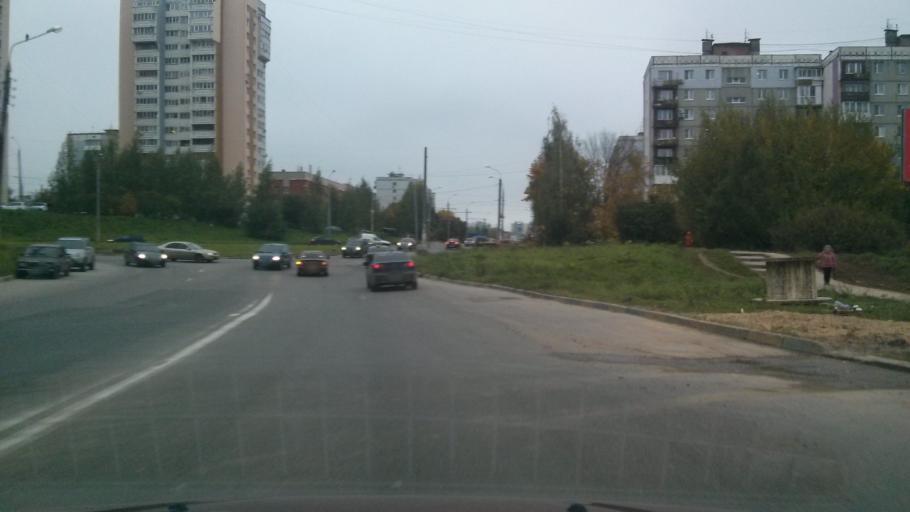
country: RU
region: Nizjnij Novgorod
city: Afonino
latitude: 56.2954
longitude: 44.0678
